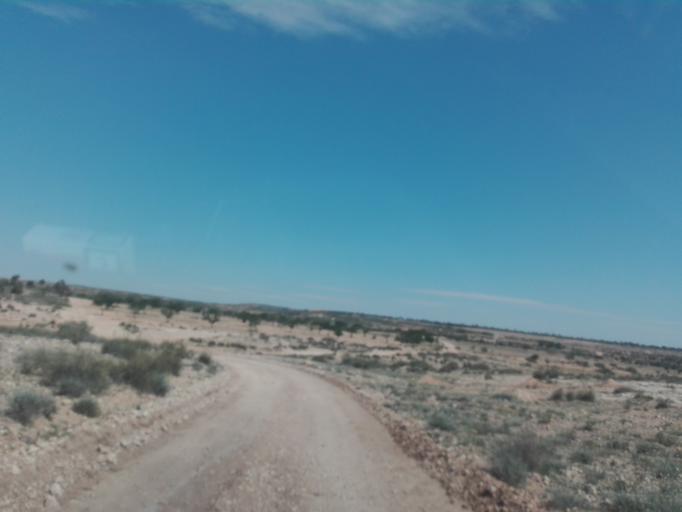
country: TN
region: Safaqis
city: Sfax
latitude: 34.6902
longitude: 10.5303
